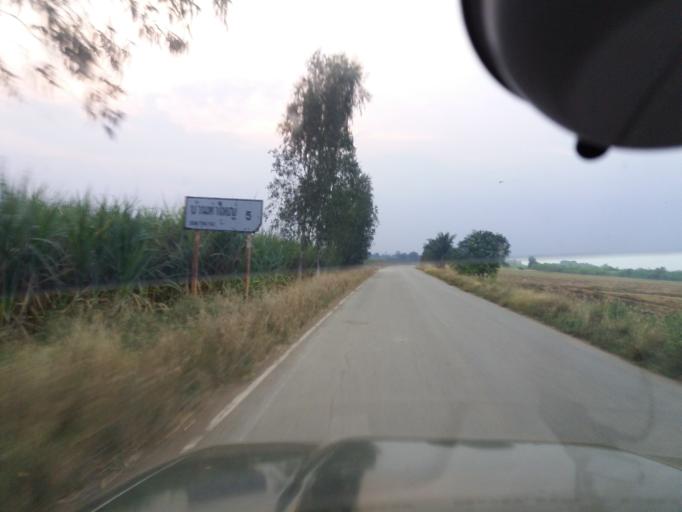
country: TH
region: Suphan Buri
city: Doem Bang Nang Buat
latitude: 14.8871
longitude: 100.1382
